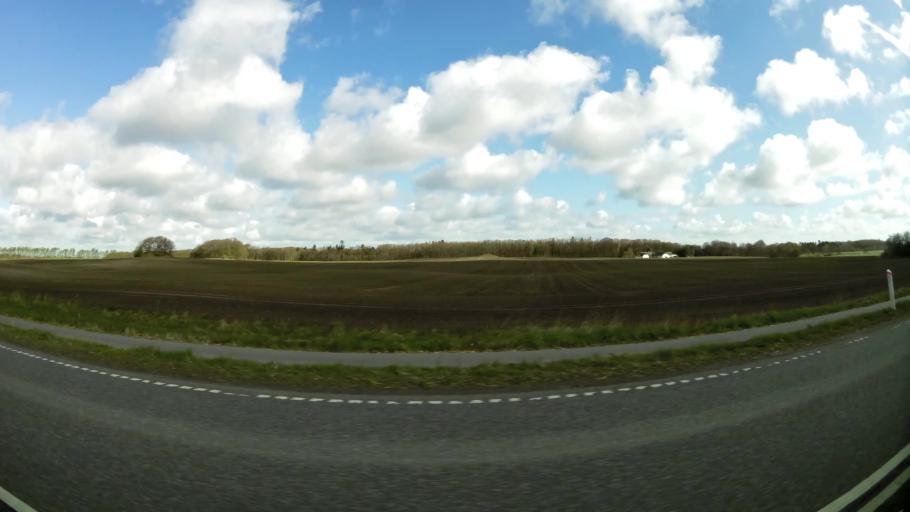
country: DK
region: North Denmark
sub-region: Mariagerfjord Kommune
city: Hobro
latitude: 56.6254
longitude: 9.8445
